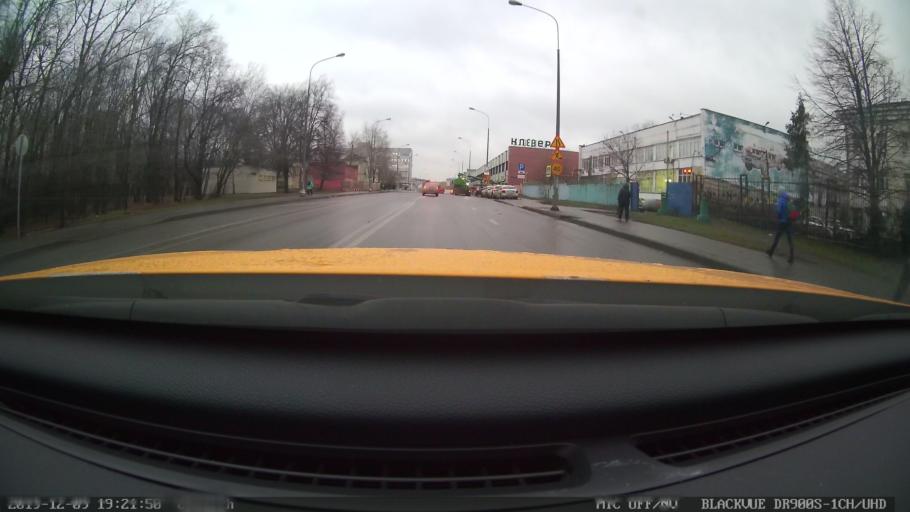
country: RU
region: Moscow
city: Ryazanskiy
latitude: 55.7557
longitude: 37.7520
